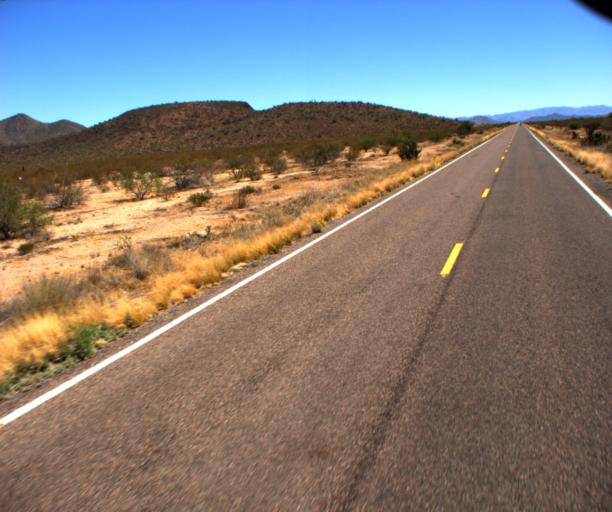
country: US
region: Arizona
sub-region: Yavapai County
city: Congress
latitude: 34.0040
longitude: -113.1167
